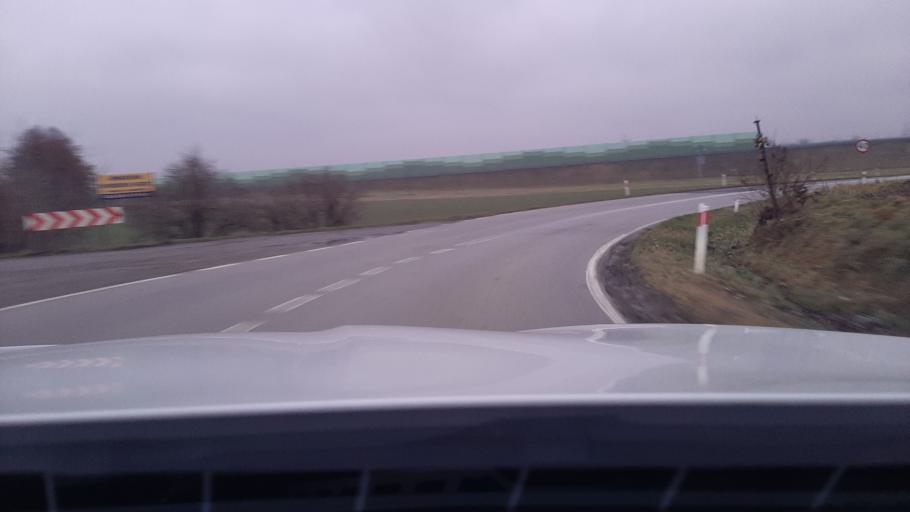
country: PL
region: Lublin Voivodeship
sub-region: Powiat lubelski
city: Garbow
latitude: 51.3483
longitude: 22.3660
